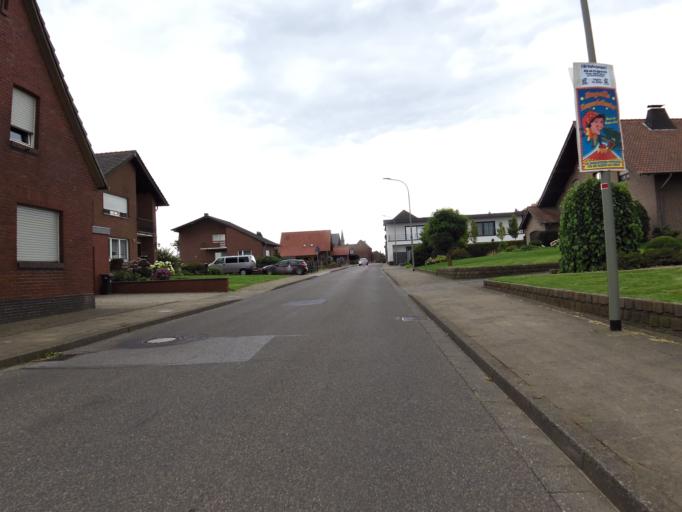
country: DE
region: North Rhine-Westphalia
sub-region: Regierungsbezirk Koln
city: Gangelt
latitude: 51.0083
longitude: 5.9694
